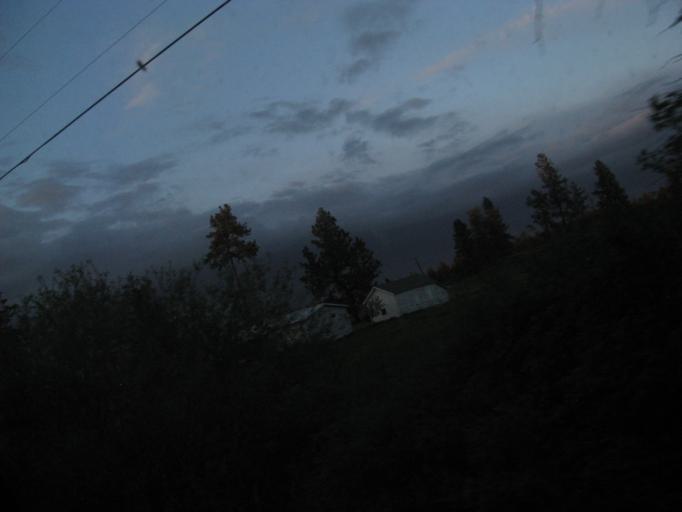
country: US
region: Washington
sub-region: Spokane County
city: Cheney
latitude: 47.4622
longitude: -117.6076
